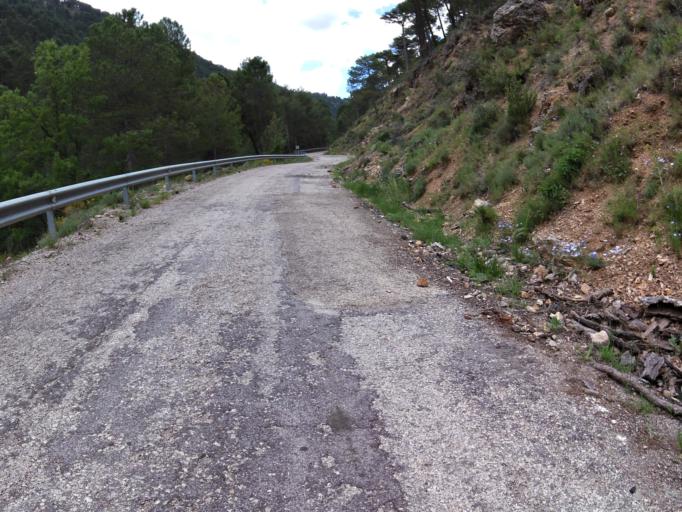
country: ES
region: Castille-La Mancha
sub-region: Provincia de Albacete
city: Paterna del Madera
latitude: 38.5695
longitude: -2.3606
